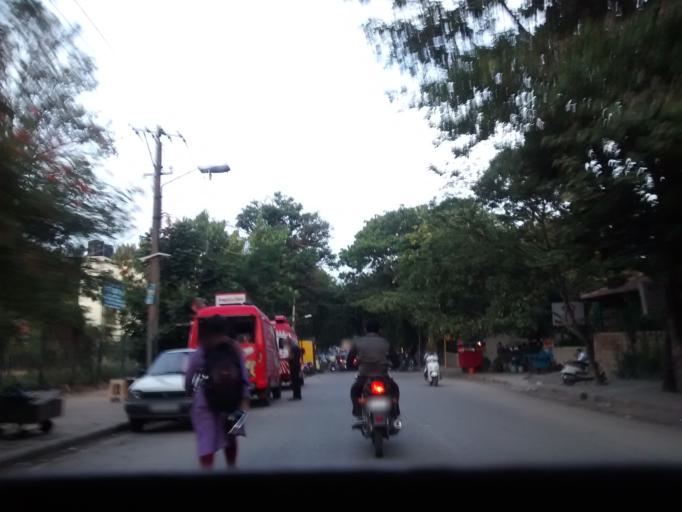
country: IN
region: Karnataka
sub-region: Bangalore Urban
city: Bangalore
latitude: 12.9739
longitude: 77.6443
